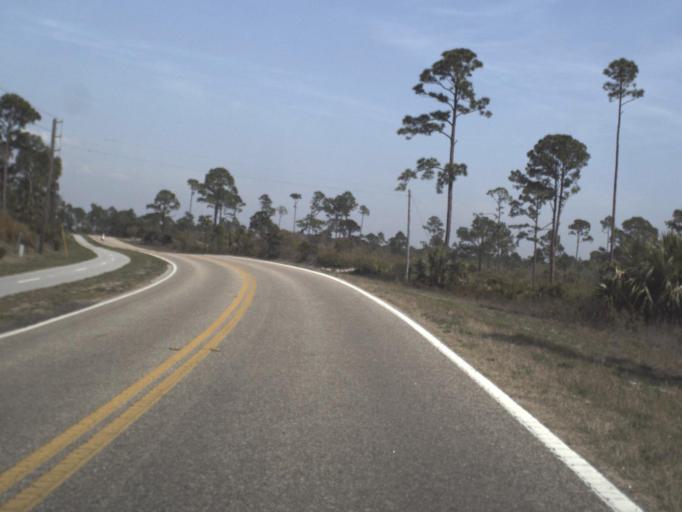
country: US
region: Florida
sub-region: Gulf County
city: Port Saint Joe
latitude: 29.6774
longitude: -85.3417
